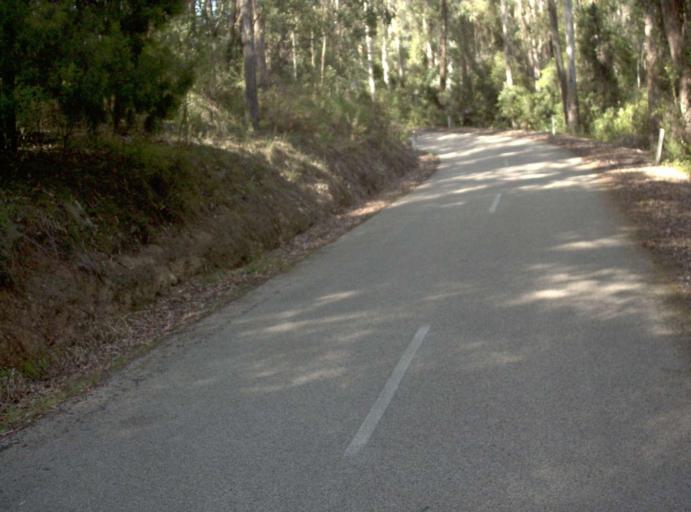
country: AU
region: Victoria
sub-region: East Gippsland
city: Lakes Entrance
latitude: -37.4395
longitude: 148.5904
